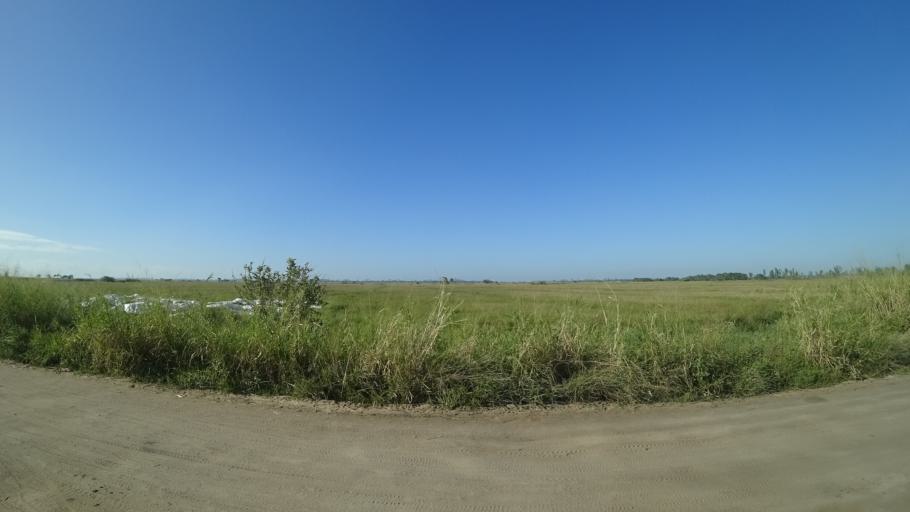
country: MZ
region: Sofala
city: Beira
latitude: -19.7630
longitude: 34.9046
